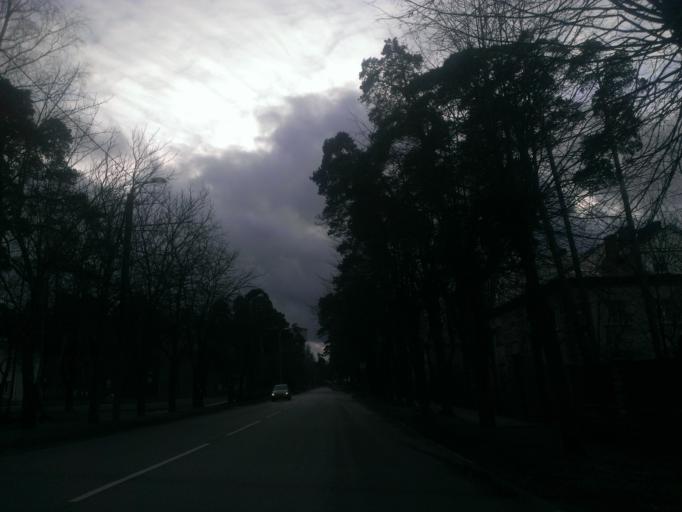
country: LV
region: Riga
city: Bolderaja
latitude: 57.0456
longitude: 24.0930
